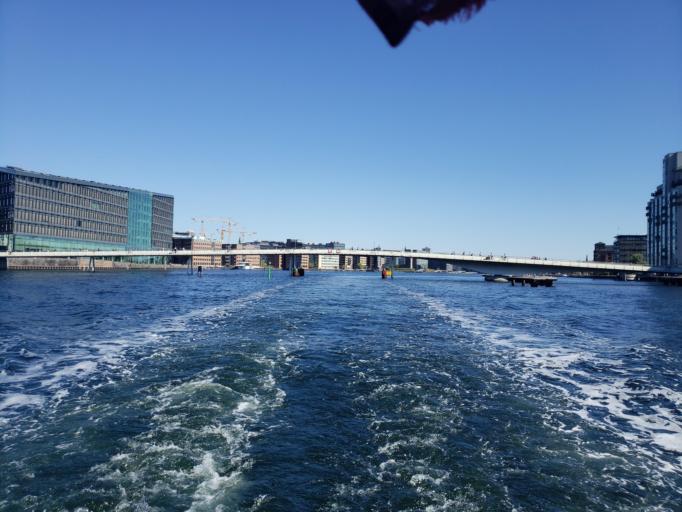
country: DK
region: Capital Region
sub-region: Kobenhavn
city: Copenhagen
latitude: 55.6604
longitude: 12.5667
